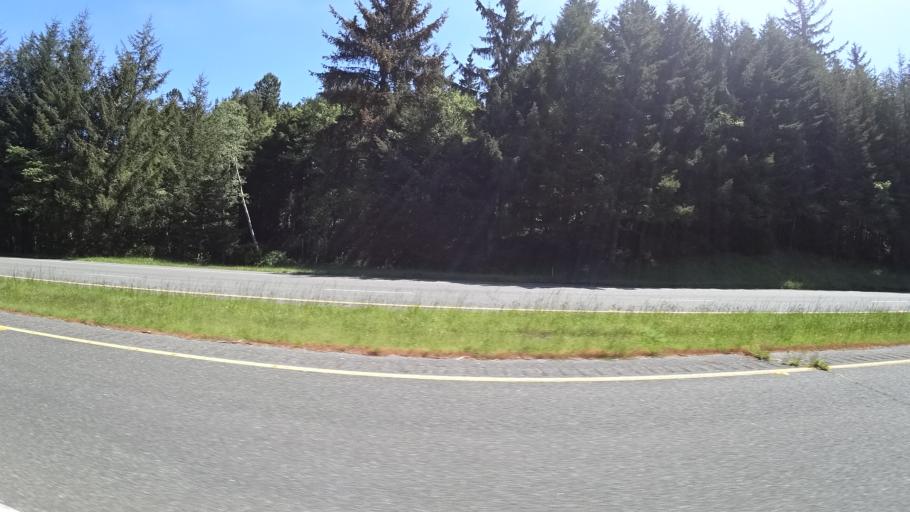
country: US
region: California
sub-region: Humboldt County
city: Westhaven-Moonstone
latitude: 41.1019
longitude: -124.1544
